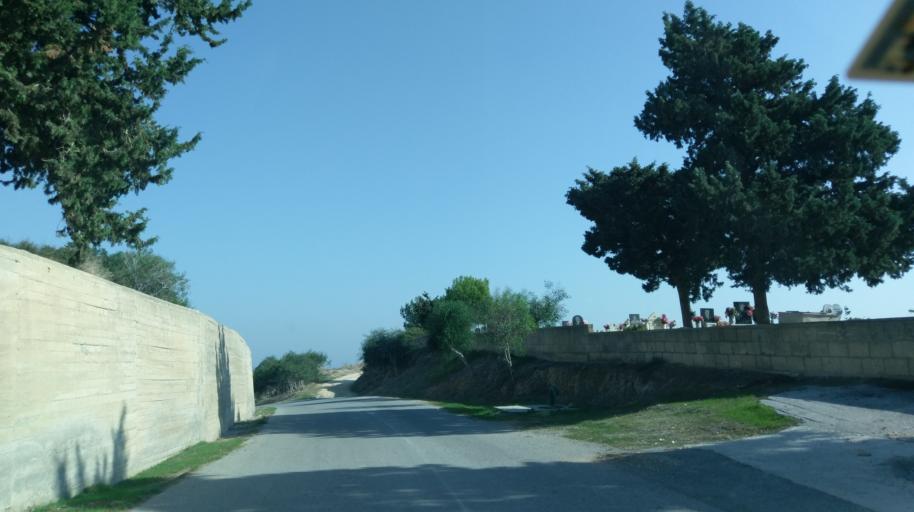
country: CY
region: Ammochostos
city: Leonarisso
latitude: 35.4903
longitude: 34.2212
